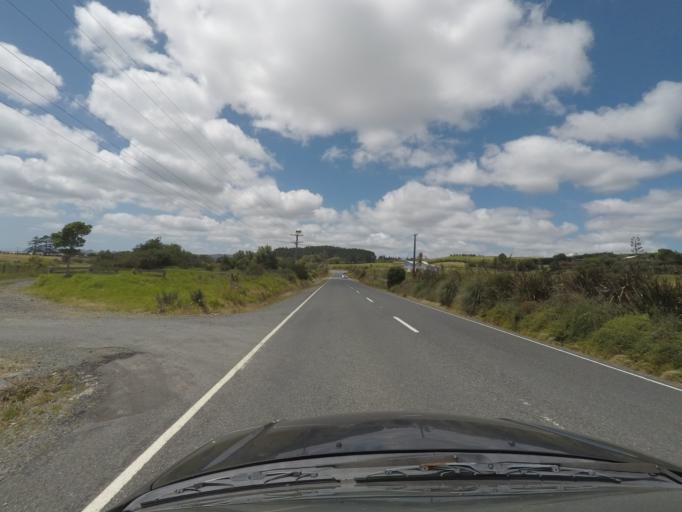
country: NZ
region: Northland
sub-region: Whangarei
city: Ruakaka
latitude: -36.0117
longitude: 174.4824
